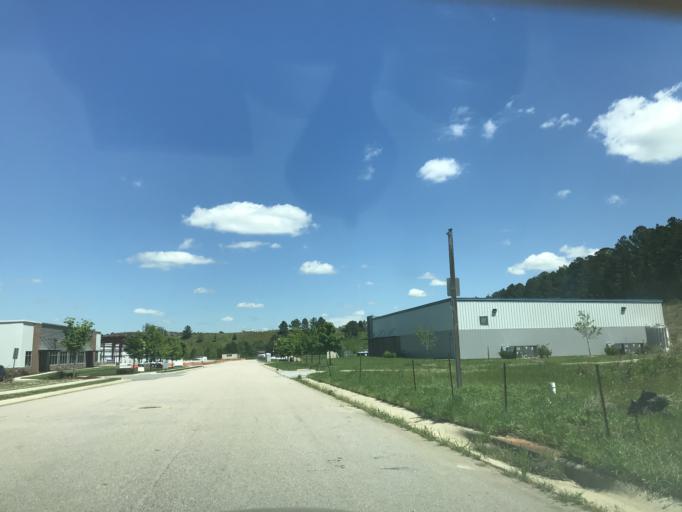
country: US
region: North Carolina
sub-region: Wake County
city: Raleigh
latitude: 35.8762
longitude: -78.5912
